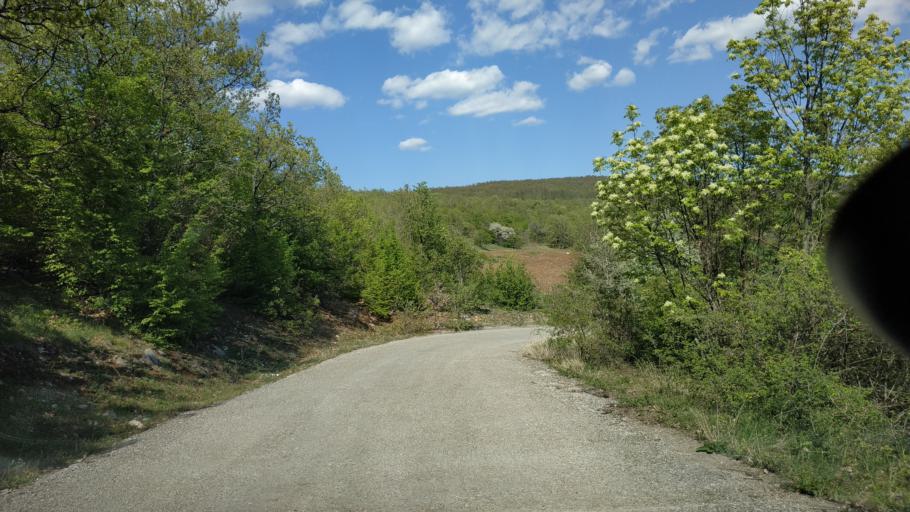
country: RS
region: Central Serbia
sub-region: Zajecarski Okrug
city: Soko Banja
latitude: 43.4989
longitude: 21.8828
